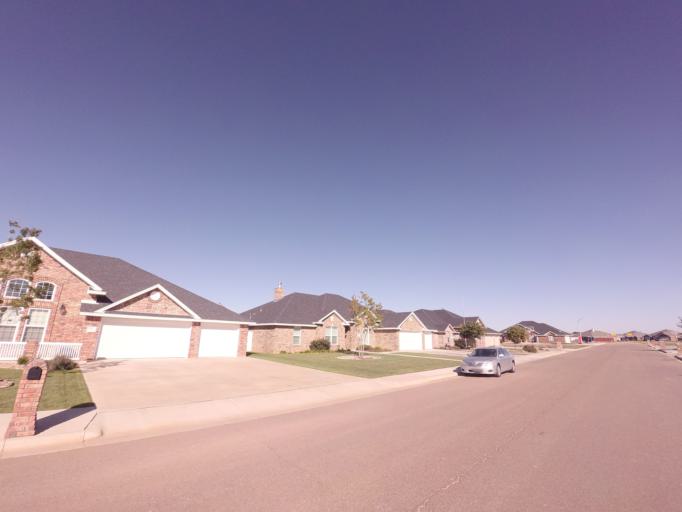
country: US
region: New Mexico
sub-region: Curry County
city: Clovis
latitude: 34.4397
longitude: -103.1703
